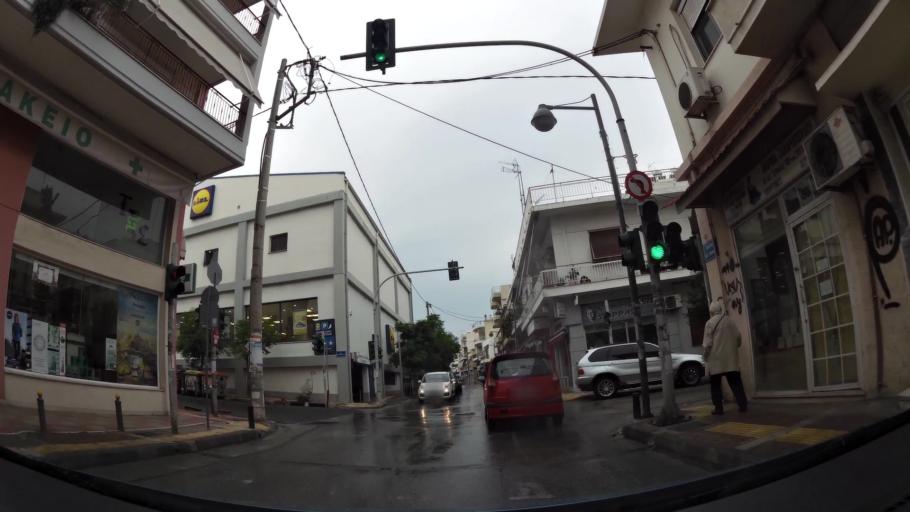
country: GR
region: Attica
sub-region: Nomarchia Athinas
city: Vyronas
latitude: 37.9576
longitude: 23.7534
